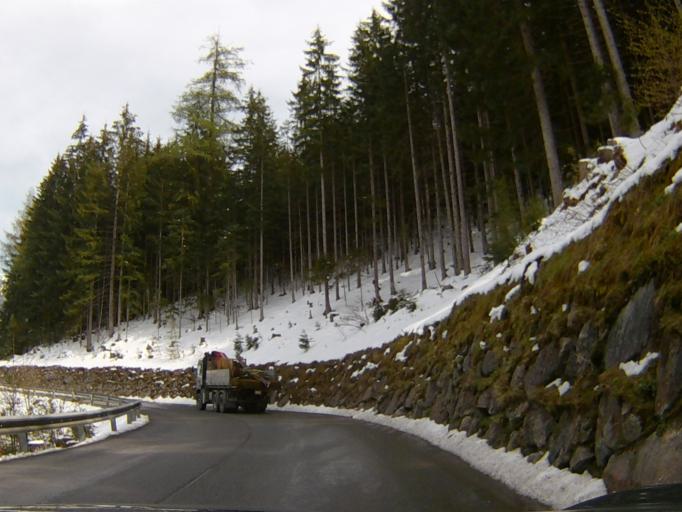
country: AT
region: Tyrol
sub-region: Politischer Bezirk Schwaz
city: Gerlosberg
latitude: 47.2135
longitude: 11.9310
